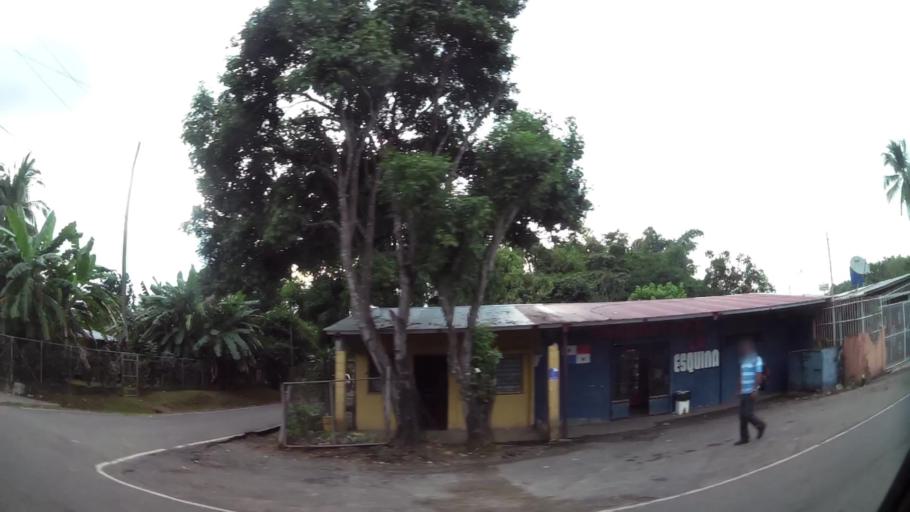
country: PA
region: Panama
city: Tocumen
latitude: 9.1011
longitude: -79.3782
